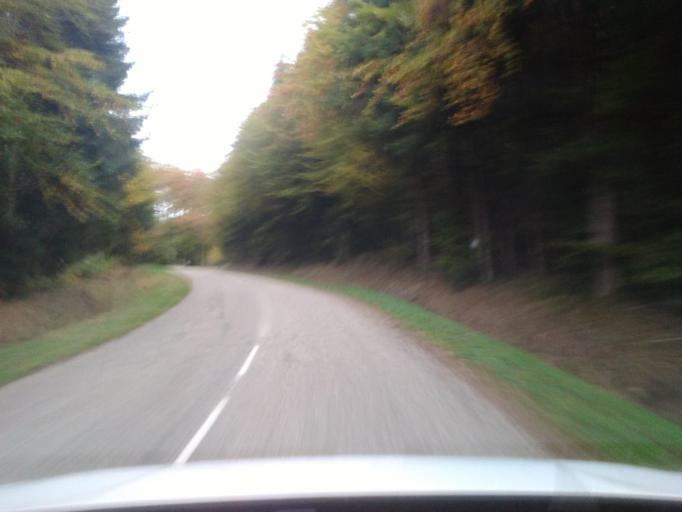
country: FR
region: Lorraine
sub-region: Departement des Vosges
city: Senones
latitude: 48.3702
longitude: 7.1047
